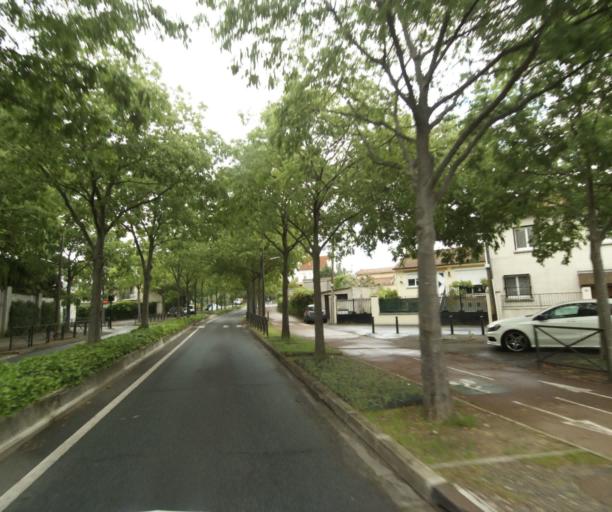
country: FR
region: Ile-de-France
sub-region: Departement du Val-d'Oise
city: Bezons
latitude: 48.9358
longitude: 2.2264
